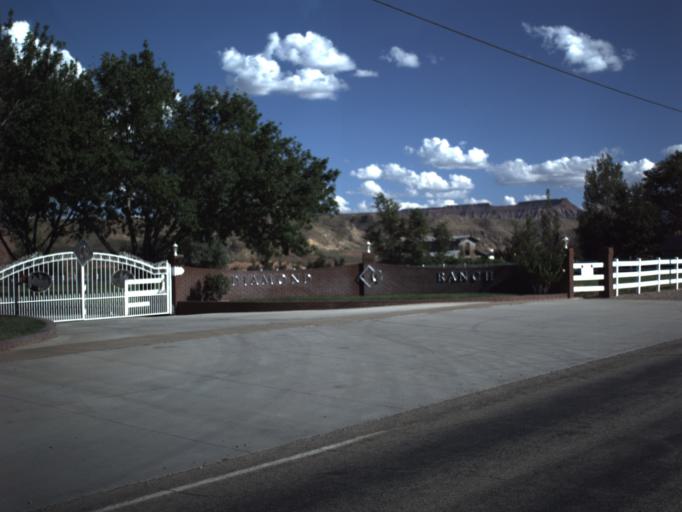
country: US
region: Utah
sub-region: Washington County
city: Toquerville
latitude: 37.2344
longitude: -113.2810
